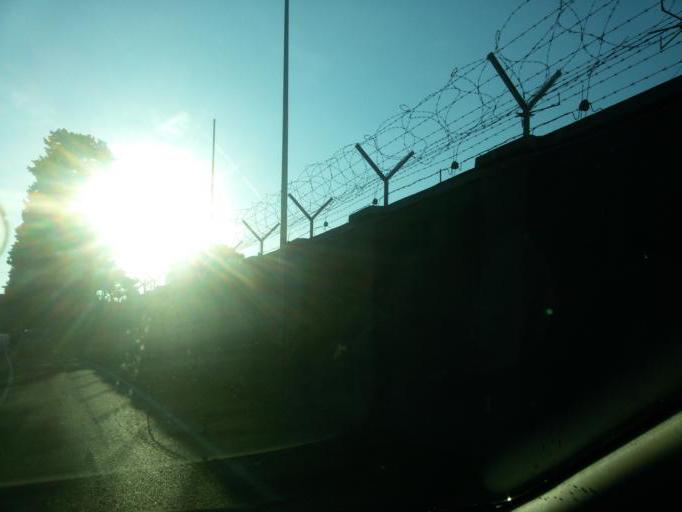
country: IT
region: Apulia
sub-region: Provincia di Brindisi
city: Materdomini
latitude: 40.6509
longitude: 17.9484
